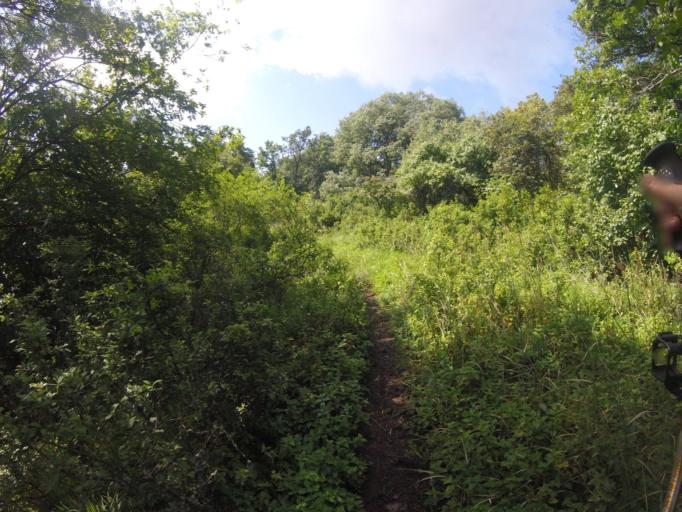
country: SK
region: Nitriansky
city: Sahy
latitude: 47.9805
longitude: 18.8879
